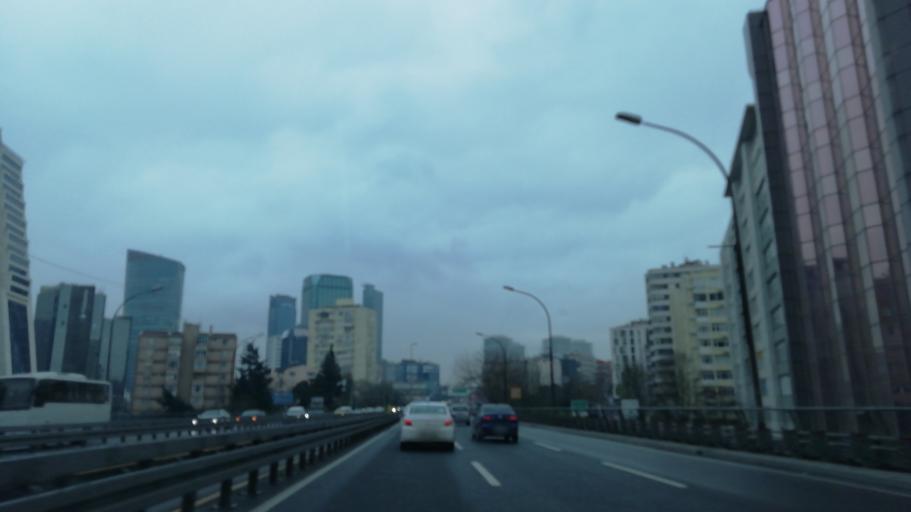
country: TR
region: Istanbul
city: Sisli
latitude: 41.0667
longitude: 29.0034
